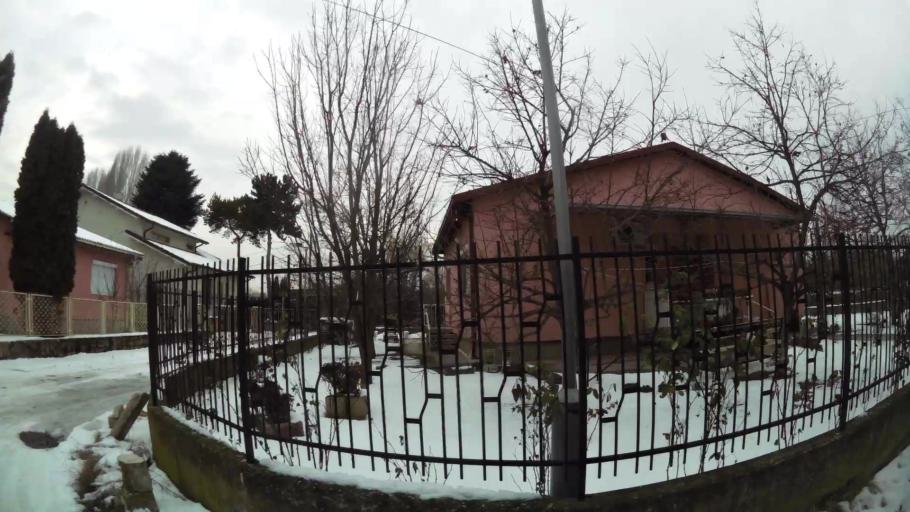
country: MK
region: Butel
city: Butel
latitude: 42.0324
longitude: 21.4404
